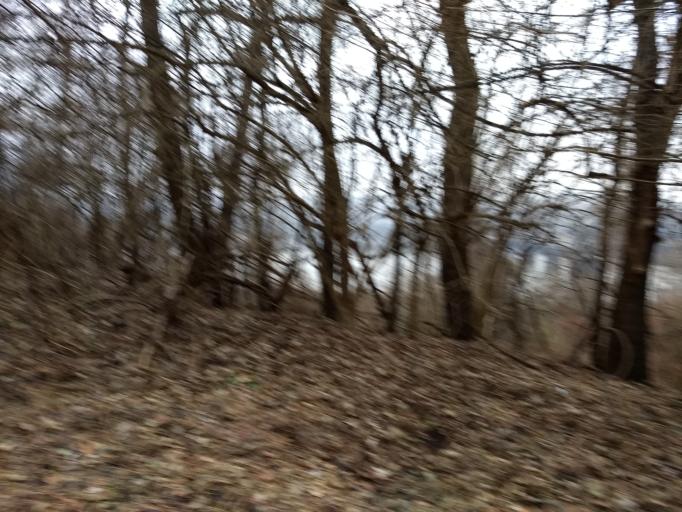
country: US
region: Pennsylvania
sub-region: Allegheny County
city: East Pittsburgh
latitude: 40.3886
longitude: -79.8477
